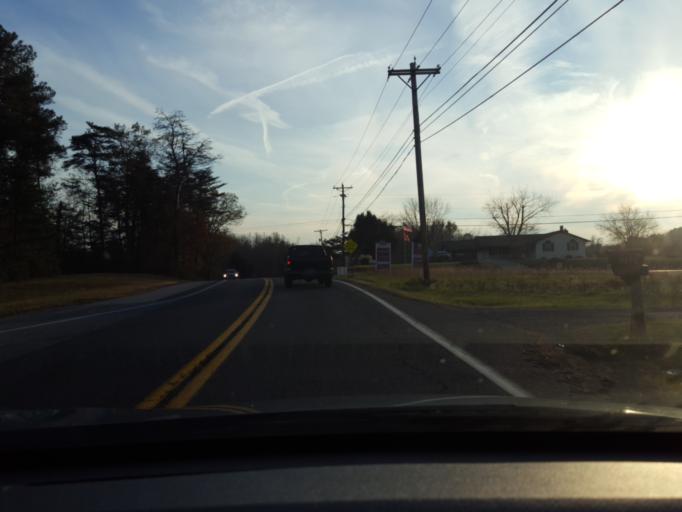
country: US
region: Maryland
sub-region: Charles County
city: Hughesville
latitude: 38.5068
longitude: -76.8645
